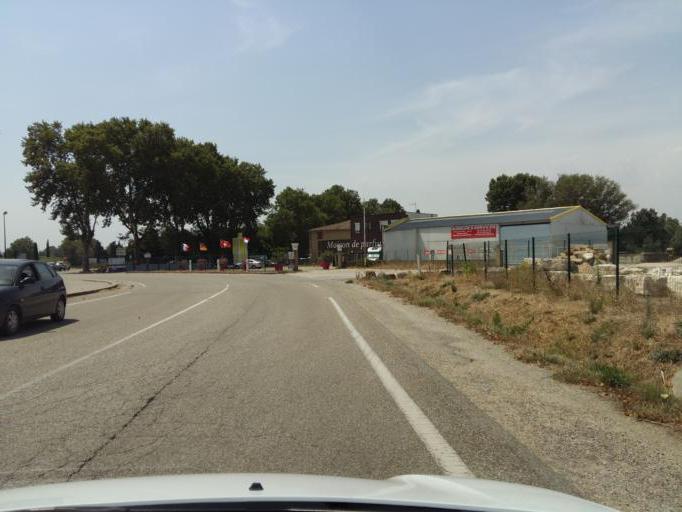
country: FR
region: Languedoc-Roussillon
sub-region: Departement du Gard
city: Pont-Saint-Esprit
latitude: 44.2620
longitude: 4.6633
